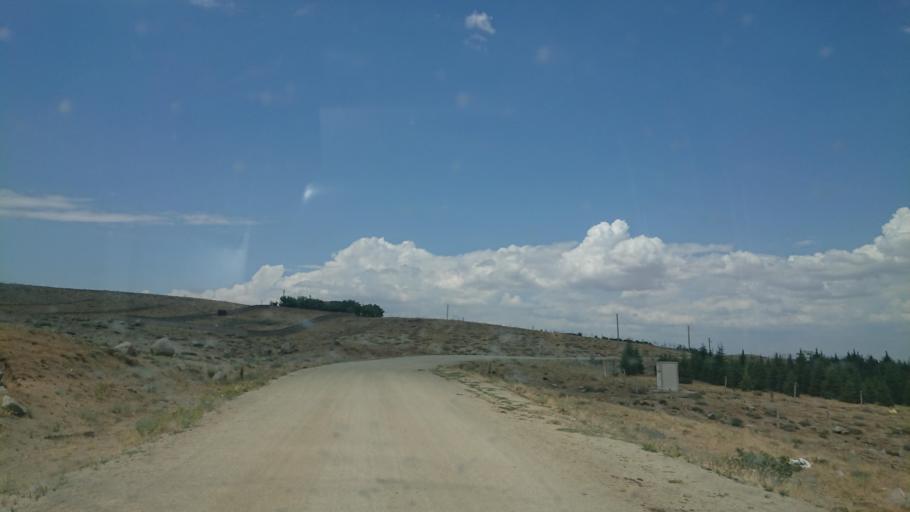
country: TR
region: Aksaray
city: Sariyahsi
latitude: 38.9487
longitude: 33.8810
